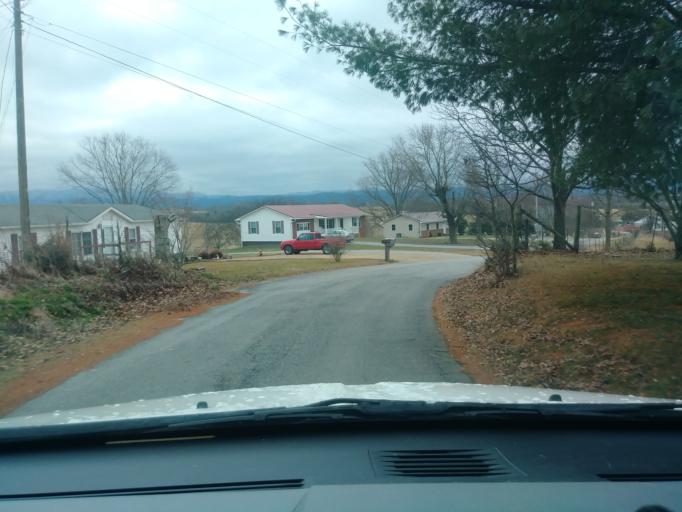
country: US
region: Tennessee
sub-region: Greene County
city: Greeneville
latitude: 36.0973
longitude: -82.8815
